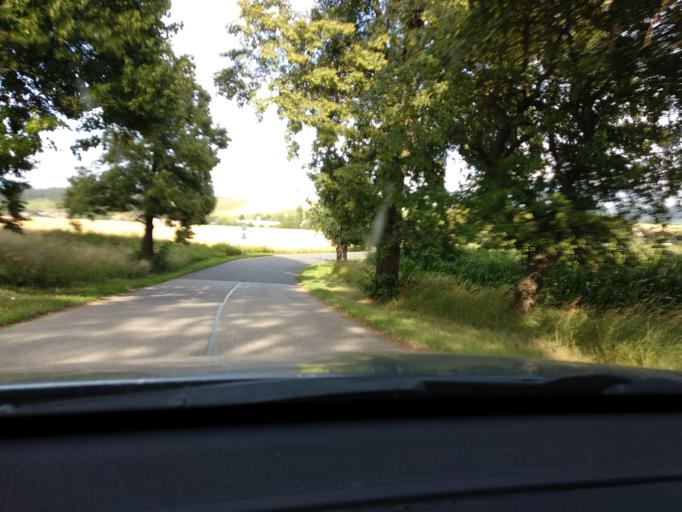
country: SK
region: Zilinsky
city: Ruzomberok
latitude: 49.0634
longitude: 19.3298
